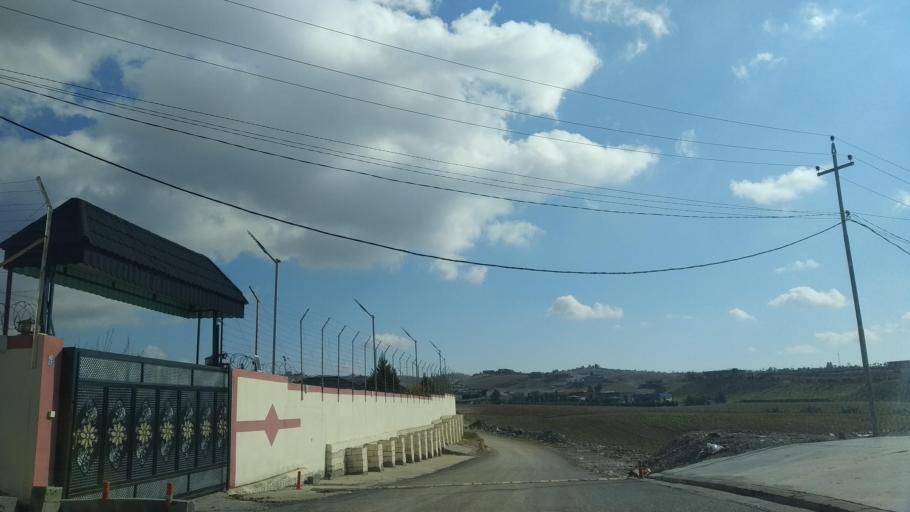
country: IQ
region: Arbil
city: Erbil
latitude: 36.2310
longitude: 44.1522
